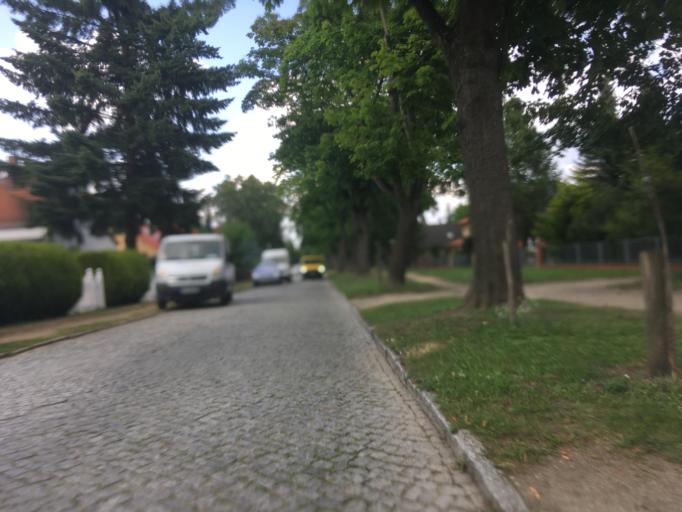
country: DE
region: Brandenburg
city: Wildau
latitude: 52.3342
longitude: 13.6236
